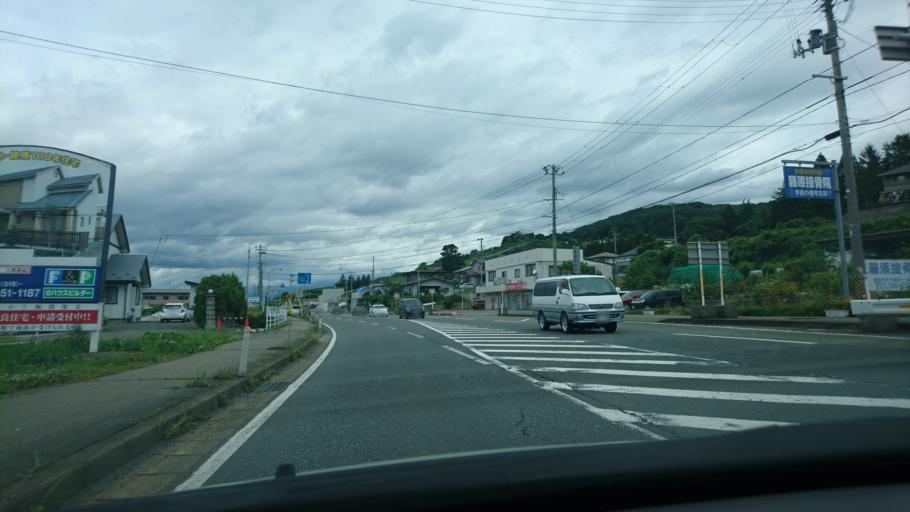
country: JP
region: Iwate
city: Morioka-shi
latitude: 39.6582
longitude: 141.1809
